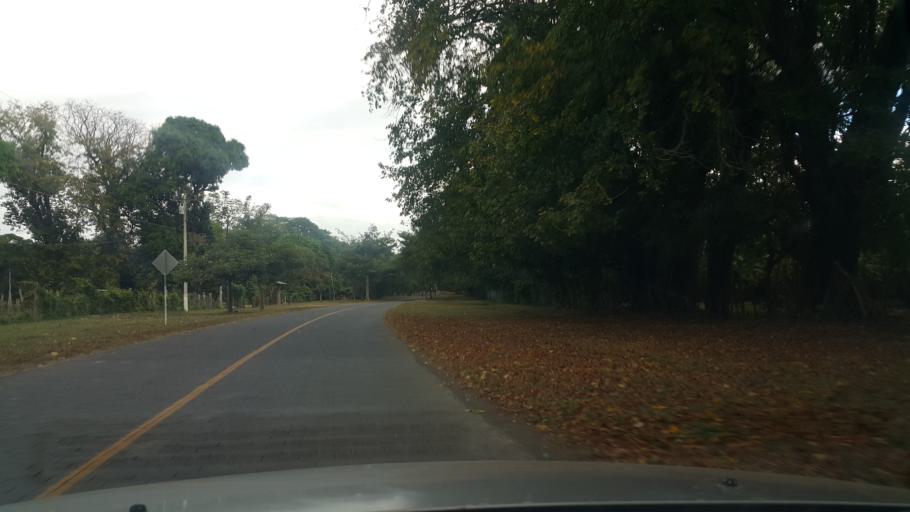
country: NI
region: Rivas
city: Moyogalpa
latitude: 11.5142
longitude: -85.7069
